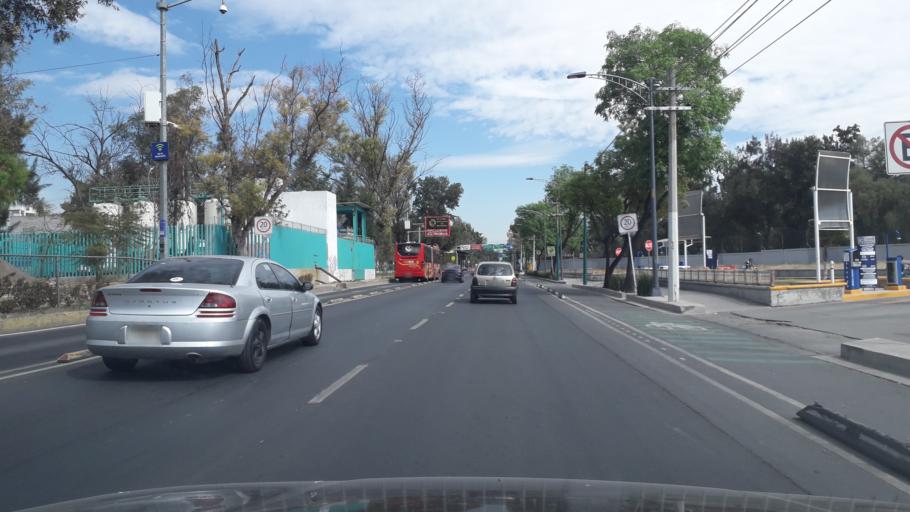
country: MX
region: Mexico City
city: Gustavo A. Madero
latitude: 19.4818
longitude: -99.0964
